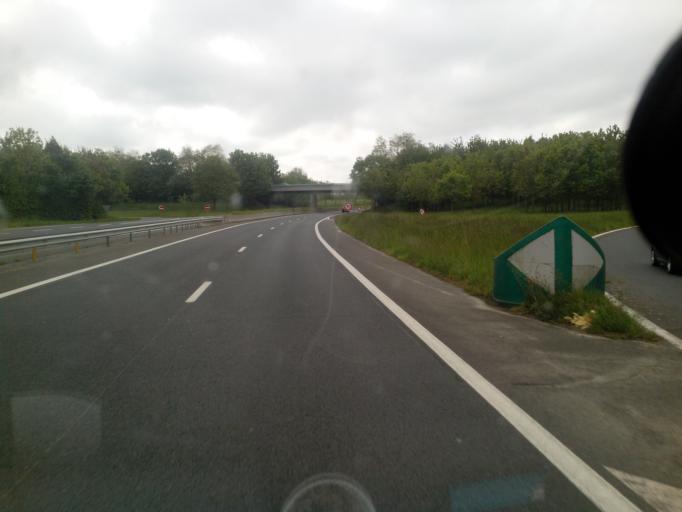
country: FR
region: Lower Normandy
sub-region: Departement du Calvados
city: Mathieu
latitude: 49.2512
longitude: -0.3797
